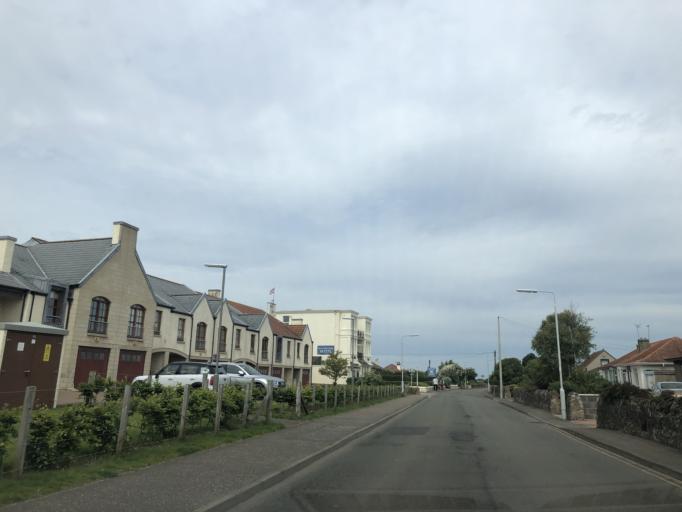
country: GB
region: Scotland
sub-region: Fife
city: Anstruther
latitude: 56.2638
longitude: -2.6223
